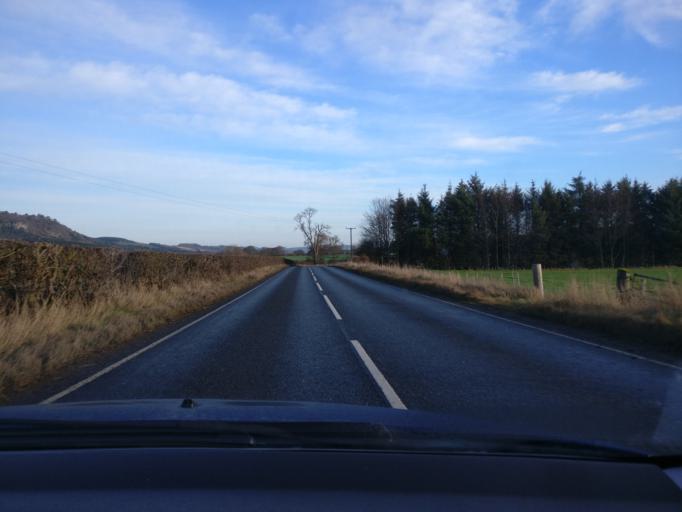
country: GB
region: Scotland
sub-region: The Scottish Borders
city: Saint Boswells
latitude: 55.4623
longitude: -2.6729
